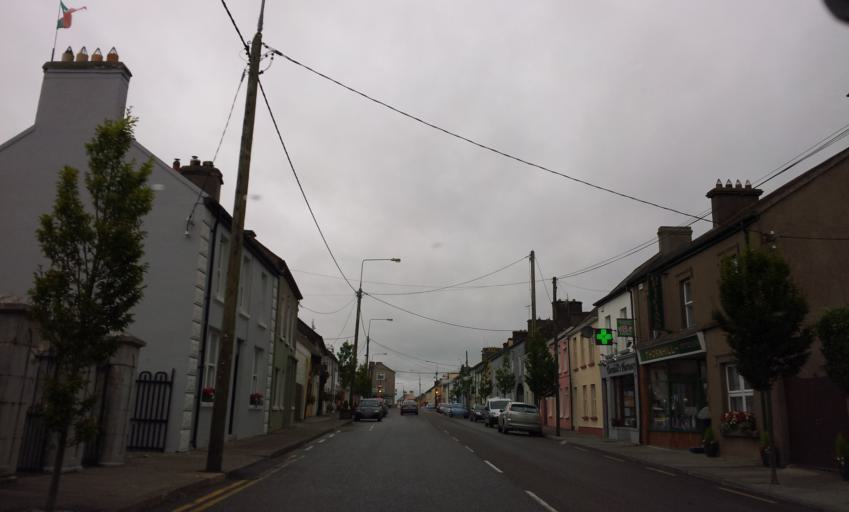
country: IE
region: Munster
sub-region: County Cork
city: Mitchelstown
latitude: 52.2464
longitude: -8.4249
